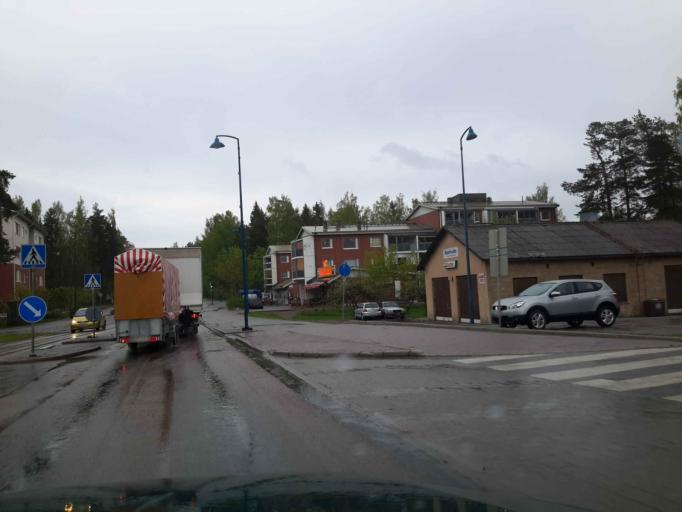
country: FI
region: Uusimaa
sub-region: Helsinki
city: Vihti
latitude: 60.3359
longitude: 24.3208
